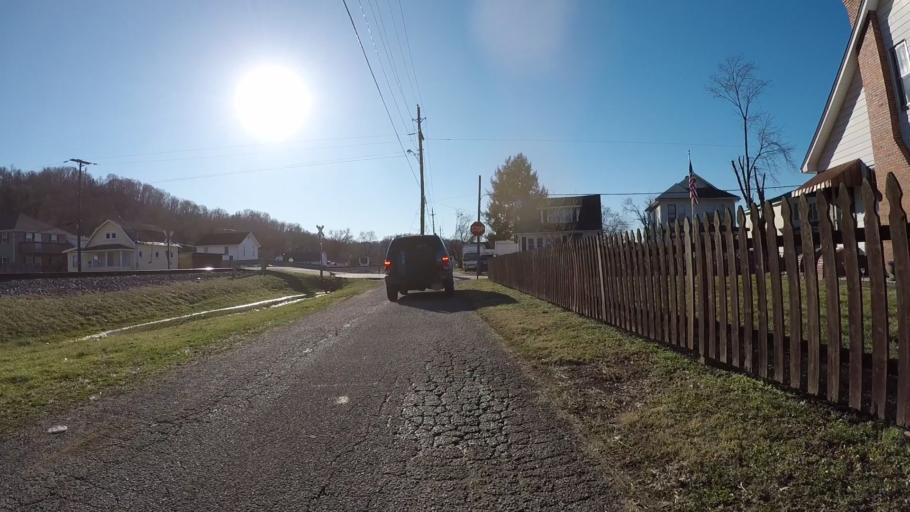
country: US
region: West Virginia
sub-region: Cabell County
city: Pea Ridge
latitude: 38.4290
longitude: -82.3768
